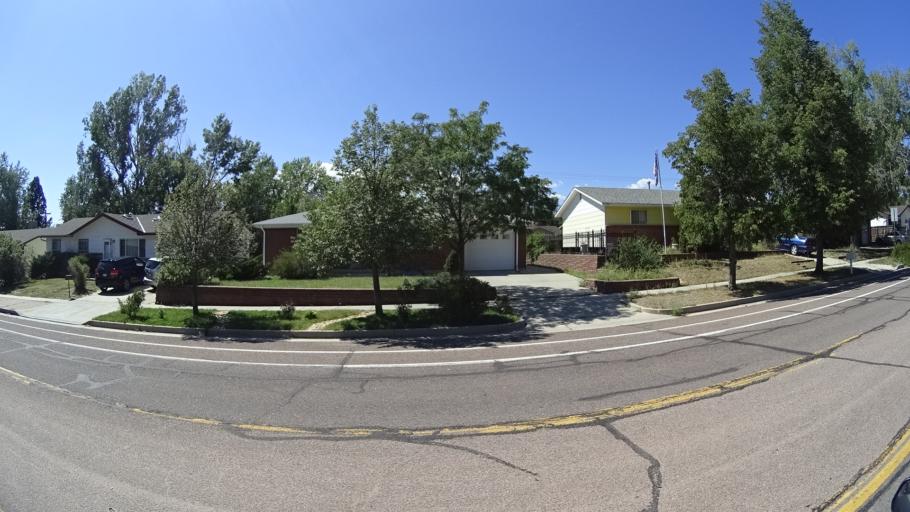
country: US
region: Colorado
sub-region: El Paso County
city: Colorado Springs
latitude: 38.8272
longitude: -104.7682
